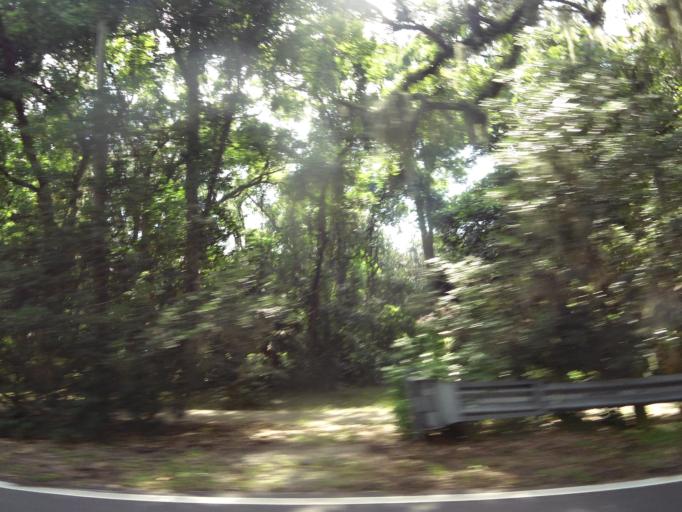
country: US
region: Florida
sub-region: Nassau County
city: Fernandina Beach
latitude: 30.5972
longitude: -81.4597
